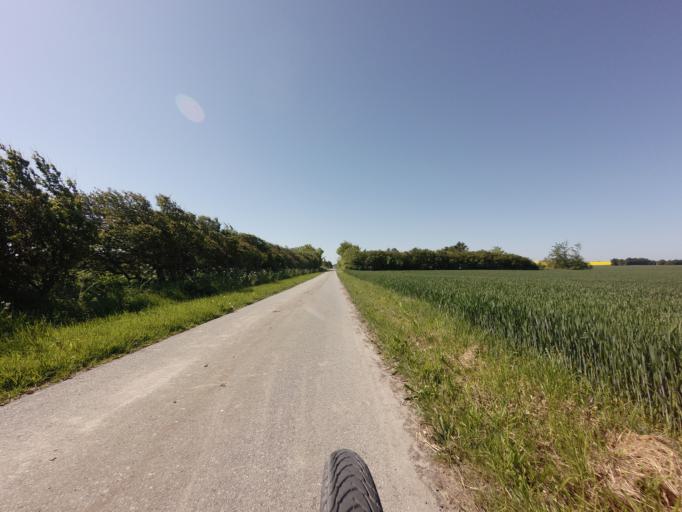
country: DK
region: North Denmark
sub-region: Hjorring Kommune
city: Vra
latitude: 57.3792
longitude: 9.8162
